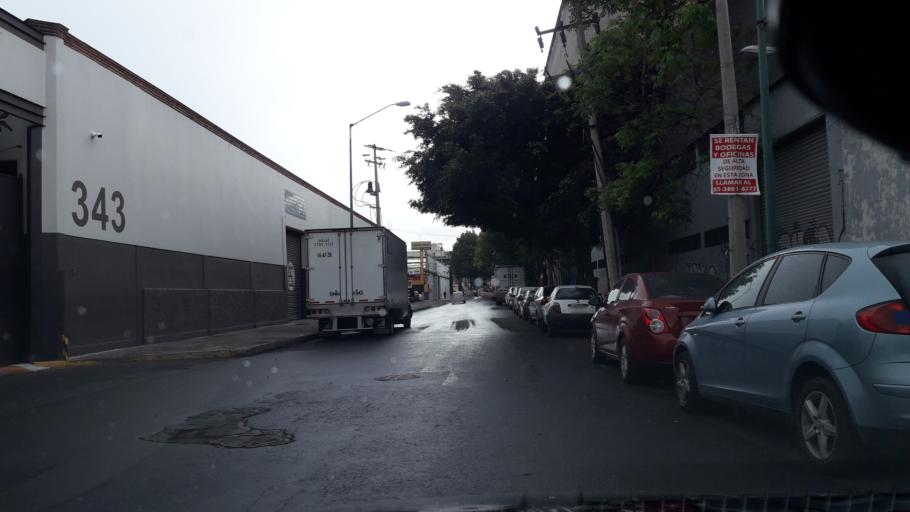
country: MX
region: Mexico City
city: Cuauhtemoc
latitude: 19.4568
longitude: -99.1548
